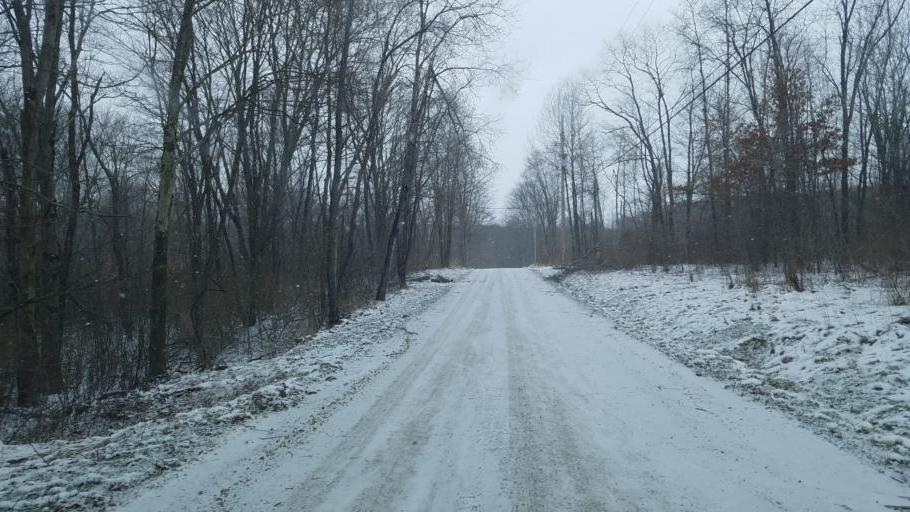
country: US
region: Pennsylvania
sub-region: Crawford County
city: Cochranton
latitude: 41.4672
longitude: -79.9857
